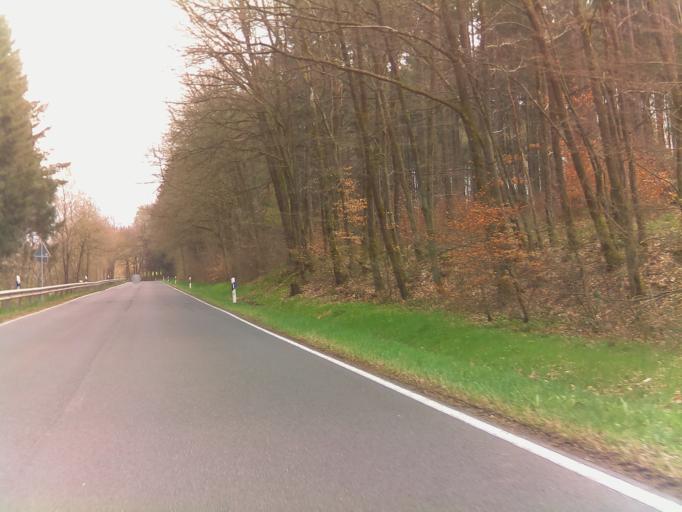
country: DE
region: Rheinland-Pfalz
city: Hausen
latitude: 49.8540
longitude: 7.3653
